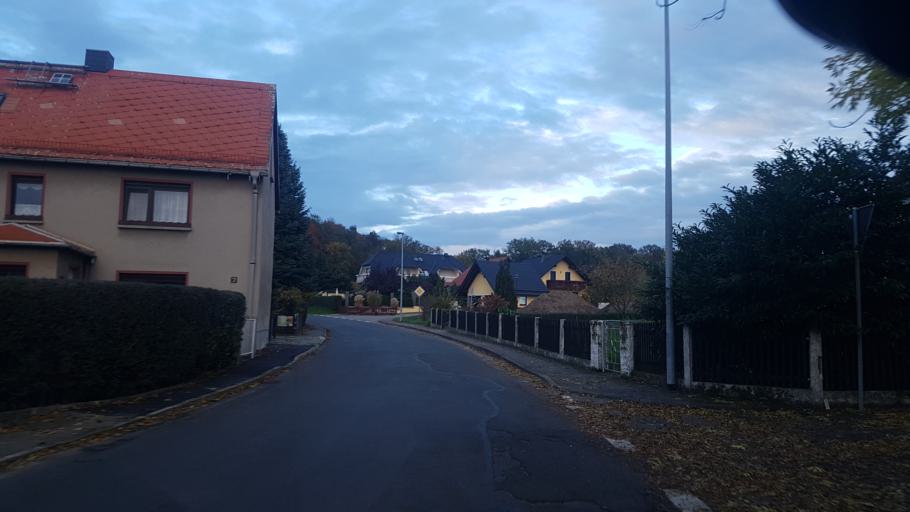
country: DE
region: Saxony
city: Cavertitz
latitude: 51.3912
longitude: 13.0952
